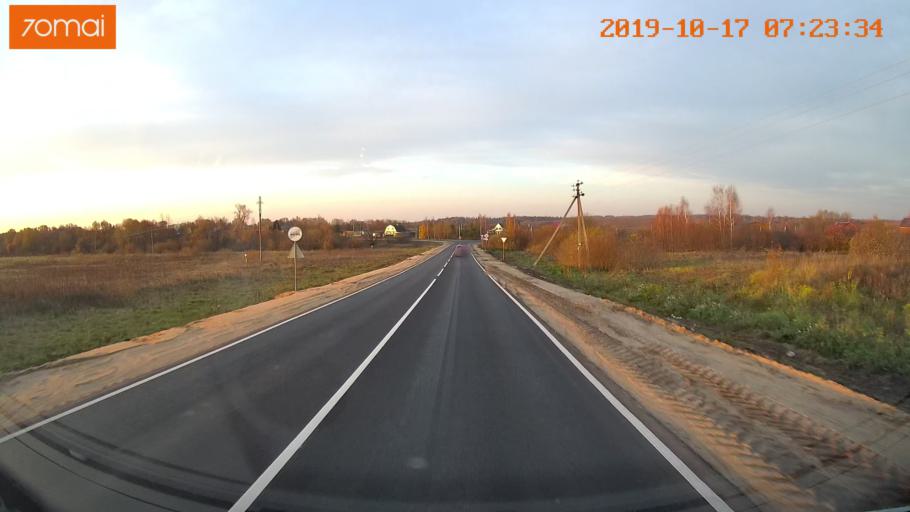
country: RU
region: Ivanovo
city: Gavrilov Posad
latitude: 56.3334
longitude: 40.1195
